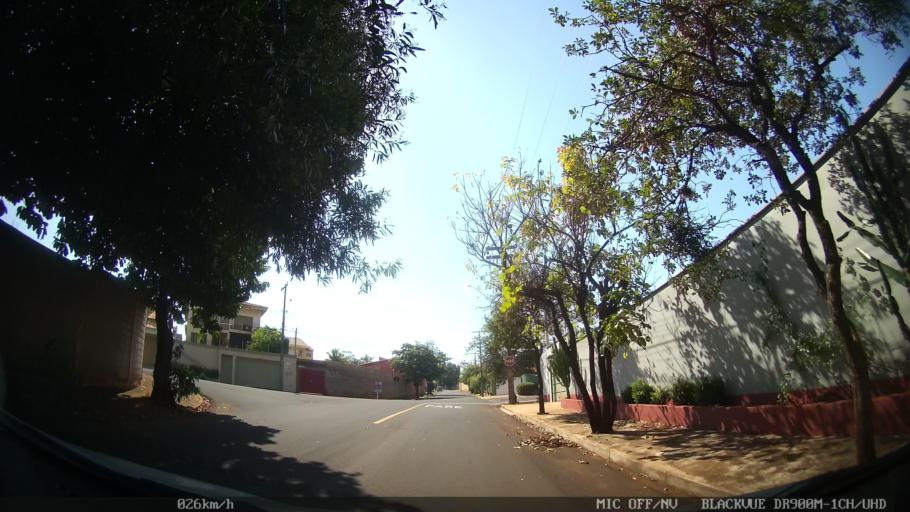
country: BR
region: Sao Paulo
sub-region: Ribeirao Preto
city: Ribeirao Preto
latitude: -21.2103
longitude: -47.7743
